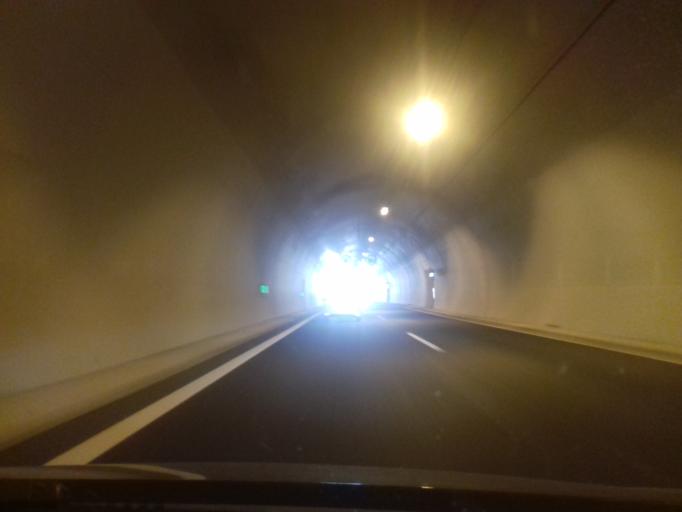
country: GR
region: West Greece
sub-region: Nomos Achaias
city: Aiyira
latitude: 38.1357
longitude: 22.3865
